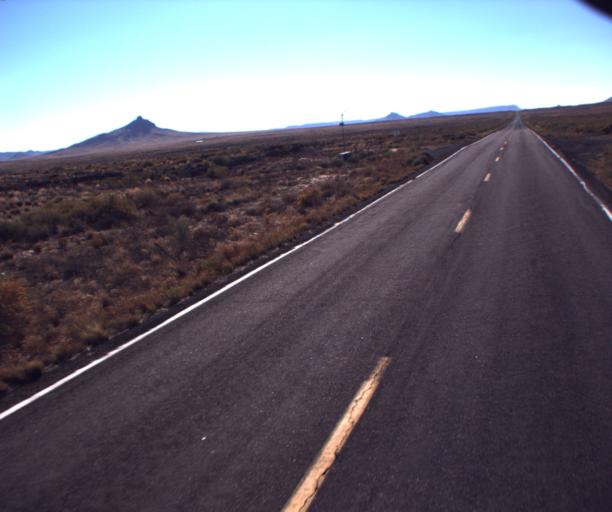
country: US
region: Arizona
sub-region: Navajo County
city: Dilkon
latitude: 35.5770
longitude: -110.4624
